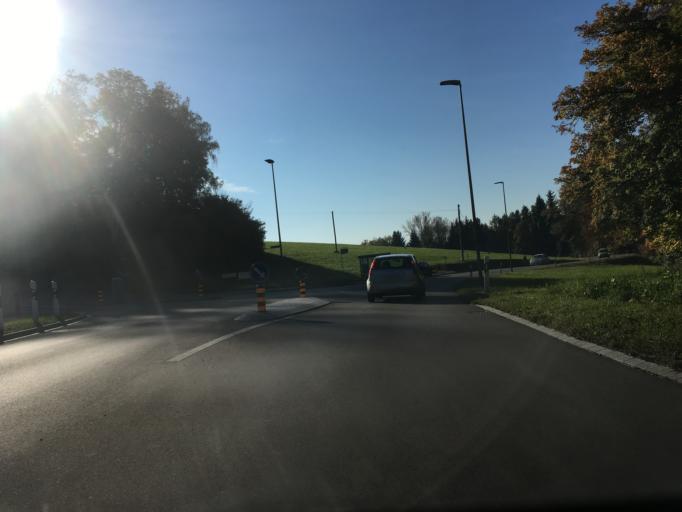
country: CH
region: Zurich
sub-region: Bezirk Dietikon
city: Uitikon
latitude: 47.3597
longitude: 8.4651
